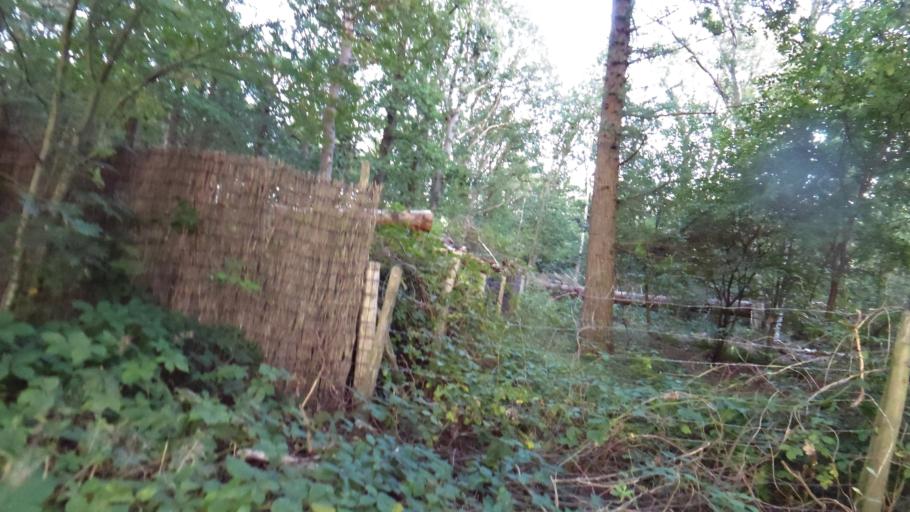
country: NL
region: Utrecht
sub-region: Gemeente Soest
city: Soest
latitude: 52.1607
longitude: 5.2397
